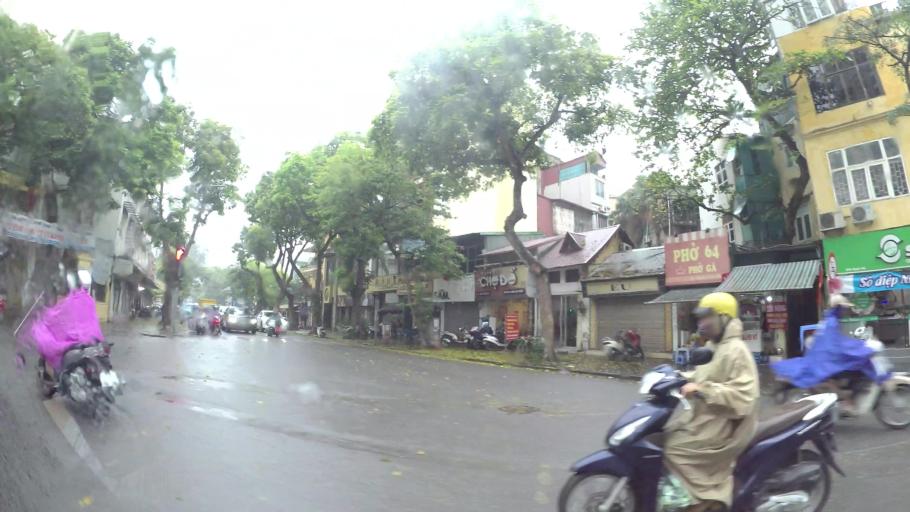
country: VN
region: Ha Noi
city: Hanoi
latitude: 21.0258
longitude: 105.8454
